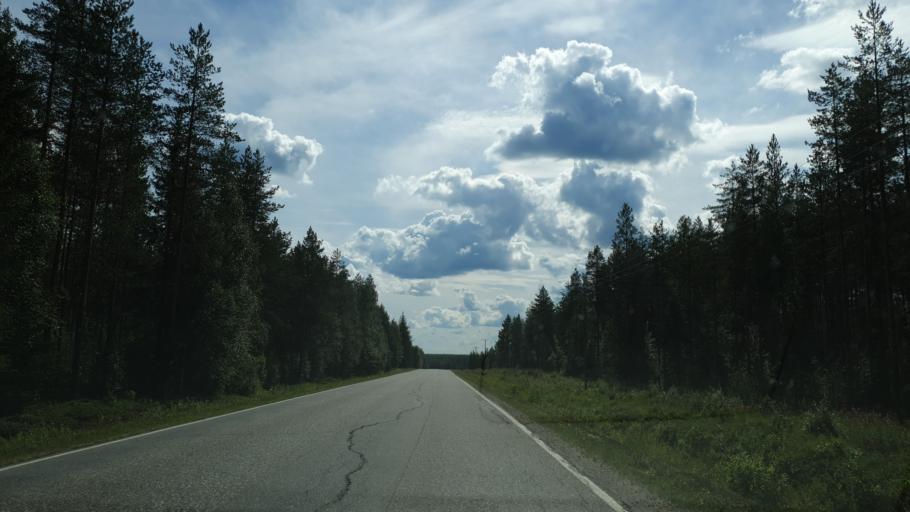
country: FI
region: Kainuu
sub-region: Kajaani
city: Sotkamo
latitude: 64.2375
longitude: 28.5007
